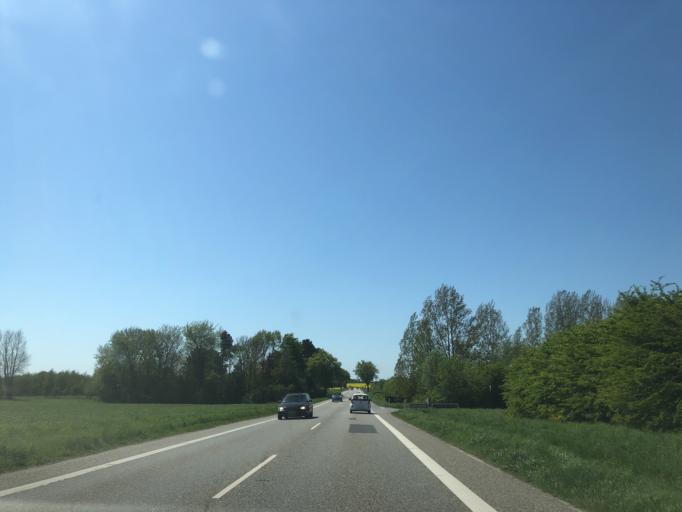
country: DK
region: Zealand
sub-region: Slagelse Kommune
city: Forlev
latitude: 55.3566
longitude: 11.2496
